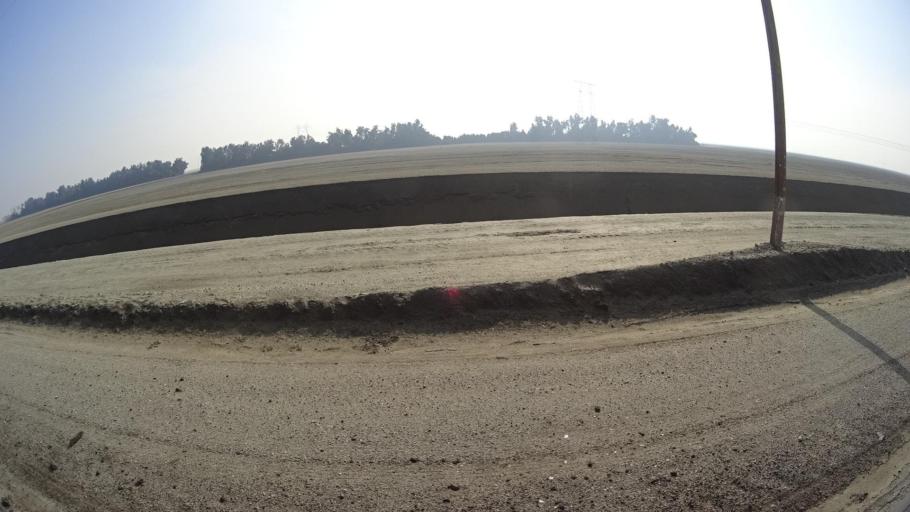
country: US
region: California
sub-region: Kern County
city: Greenfield
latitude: 35.1513
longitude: -119.0154
